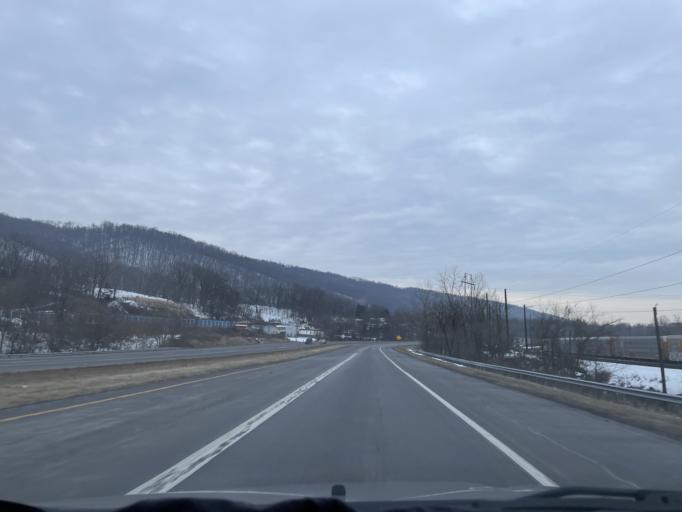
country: US
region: West Virginia
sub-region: Mineral County
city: Wiley Ford
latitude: 39.6188
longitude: -78.7315
